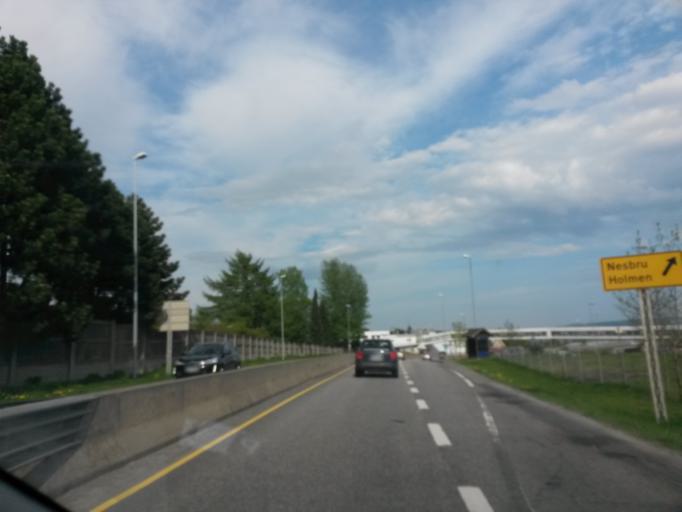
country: NO
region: Akershus
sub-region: Asker
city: Billingstad
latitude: 59.8552
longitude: 10.4852
